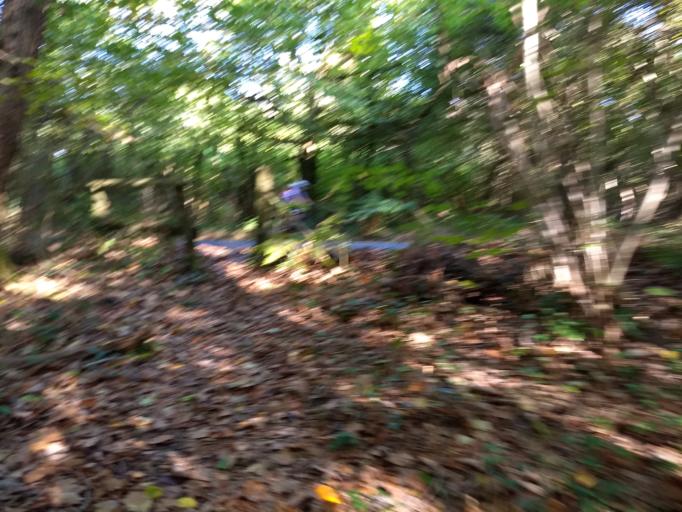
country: GB
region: England
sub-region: Isle of Wight
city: Newchurch
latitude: 50.7205
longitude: -1.2163
